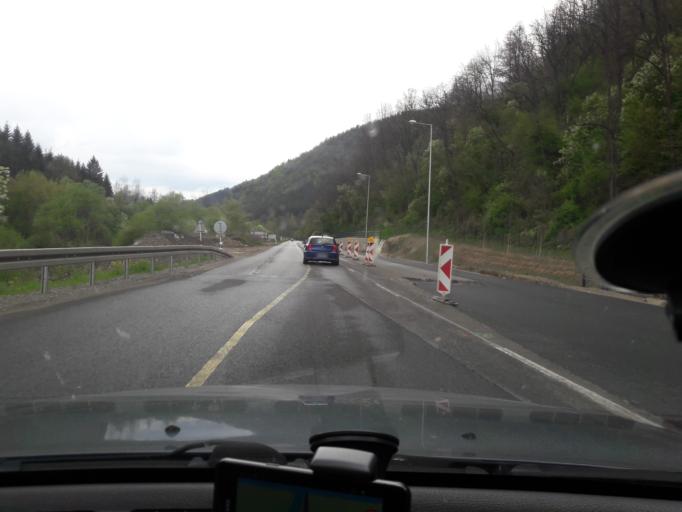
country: SK
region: Banskobystricky
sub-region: Okres Banska Bystrica
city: Brezno
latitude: 48.8084
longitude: 19.6121
